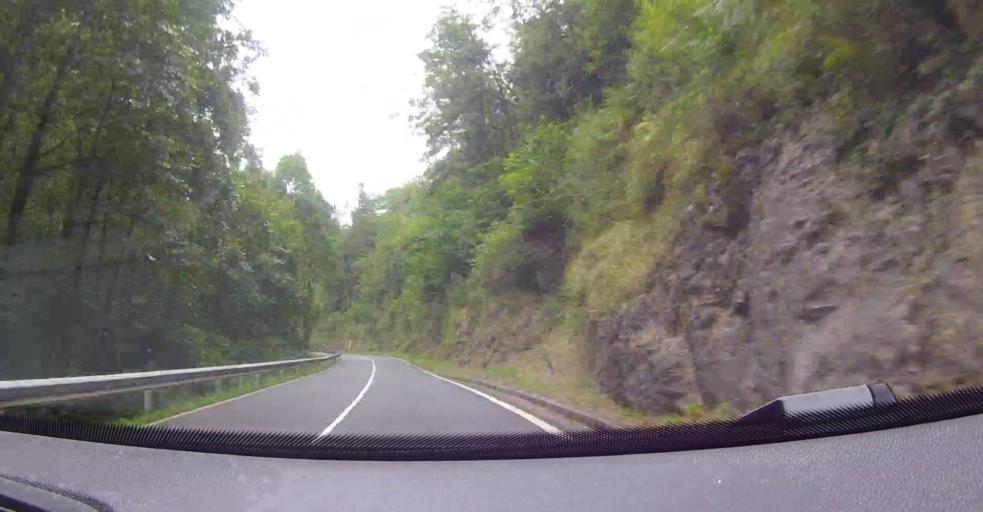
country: ES
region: Basque Country
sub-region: Bizkaia
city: Balmaseda
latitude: 43.2468
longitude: -3.2082
